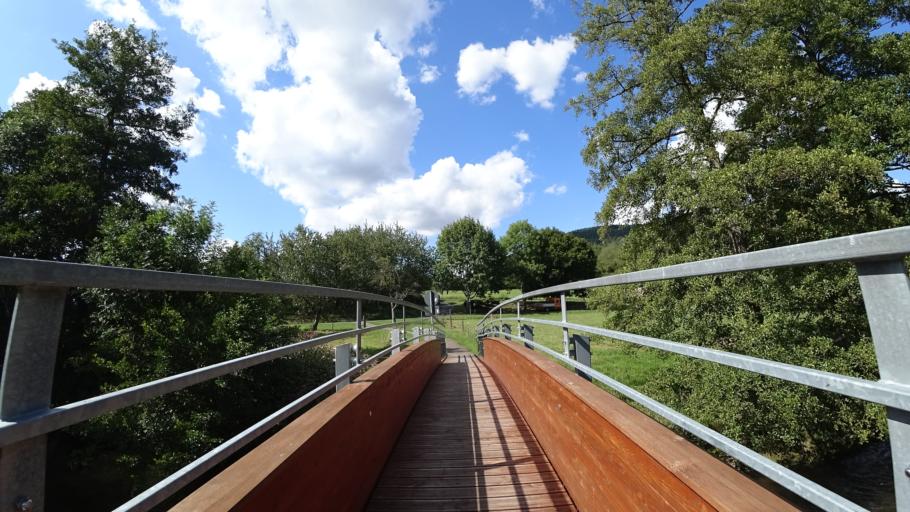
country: DE
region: Bavaria
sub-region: Regierungsbezirk Unterfranken
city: Miltenberg
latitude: 49.7053
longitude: 9.2886
